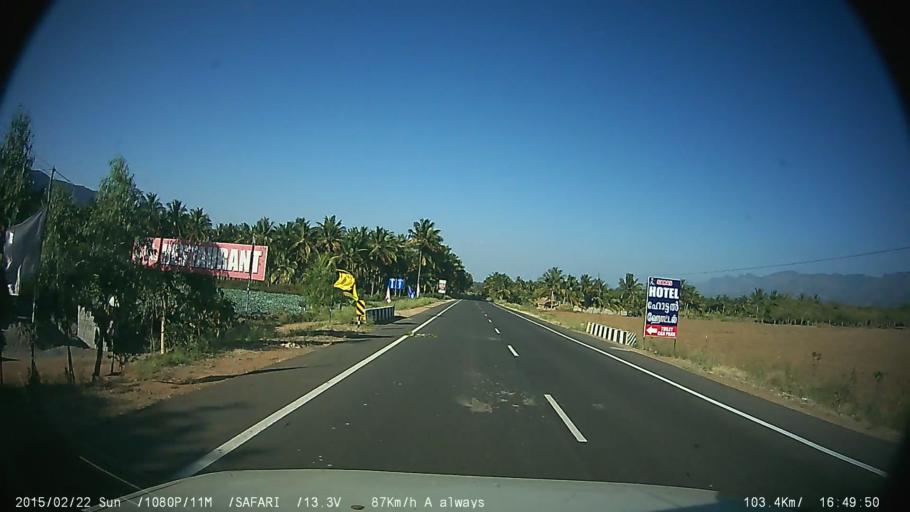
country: IN
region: Tamil Nadu
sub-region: Theni
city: Gudalur
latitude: 9.6358
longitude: 77.2048
